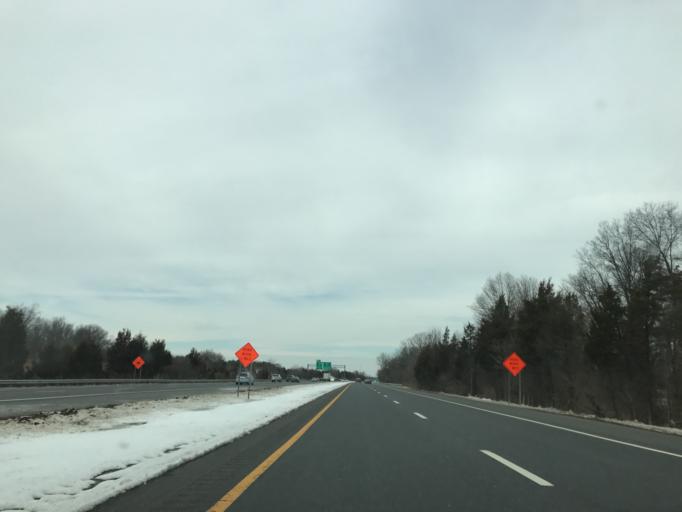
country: US
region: New Jersey
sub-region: Somerset County
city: Bridgewater
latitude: 40.6190
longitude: -74.6360
